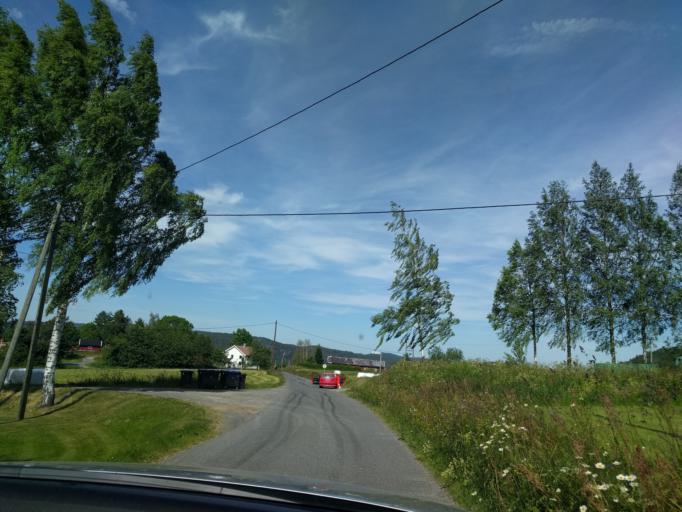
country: NO
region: Aust-Agder
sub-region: Gjerstad
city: Gjerstad
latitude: 58.8845
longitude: 8.9504
